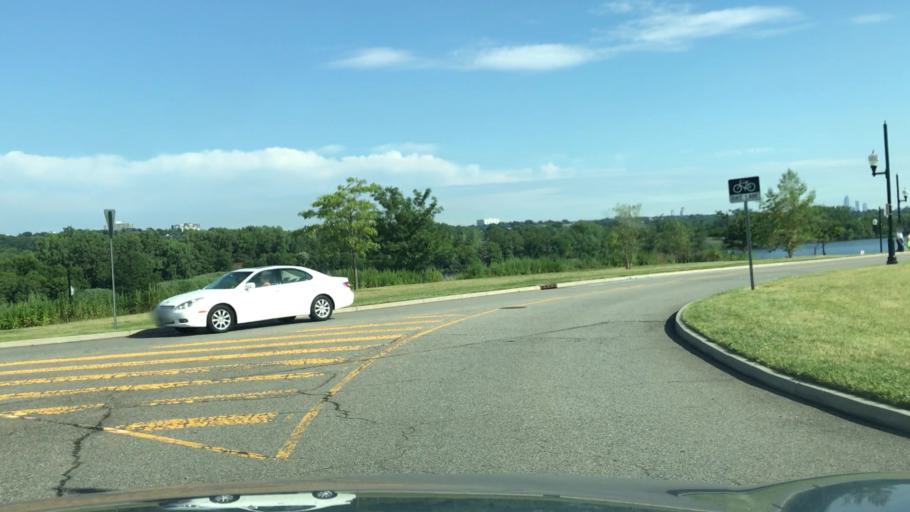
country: US
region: New Jersey
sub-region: Bergen County
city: Palisades Park
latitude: 40.8618
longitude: -74.0061
